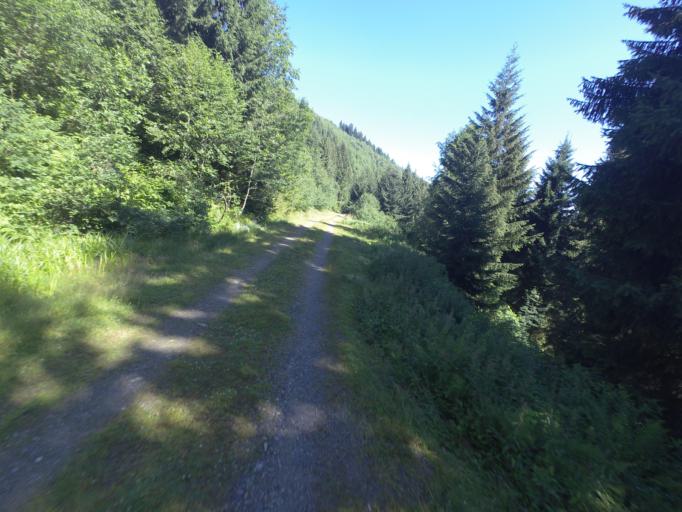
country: AT
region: Salzburg
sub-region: Politischer Bezirk Sankt Johann im Pongau
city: Sankt Veit im Pongau
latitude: 47.3496
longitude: 13.1510
